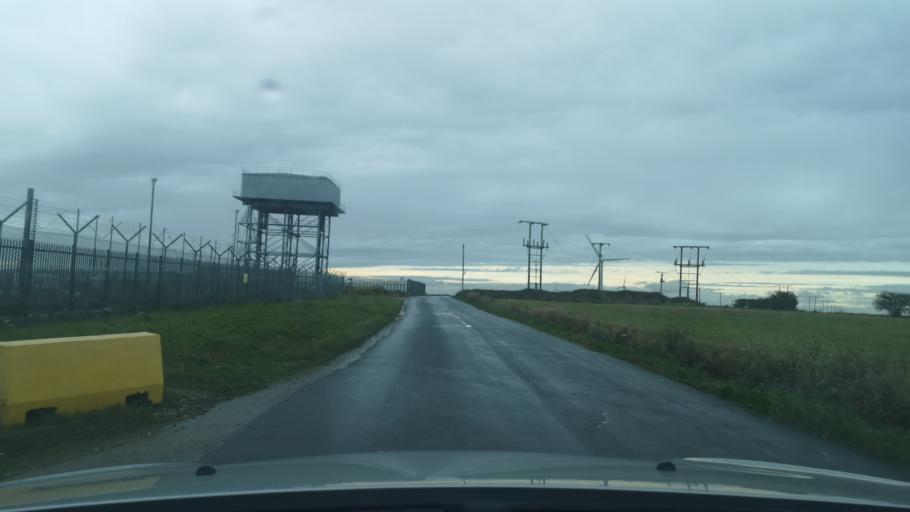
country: GB
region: England
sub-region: East Riding of Yorkshire
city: Easington
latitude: 53.6633
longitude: 0.1086
